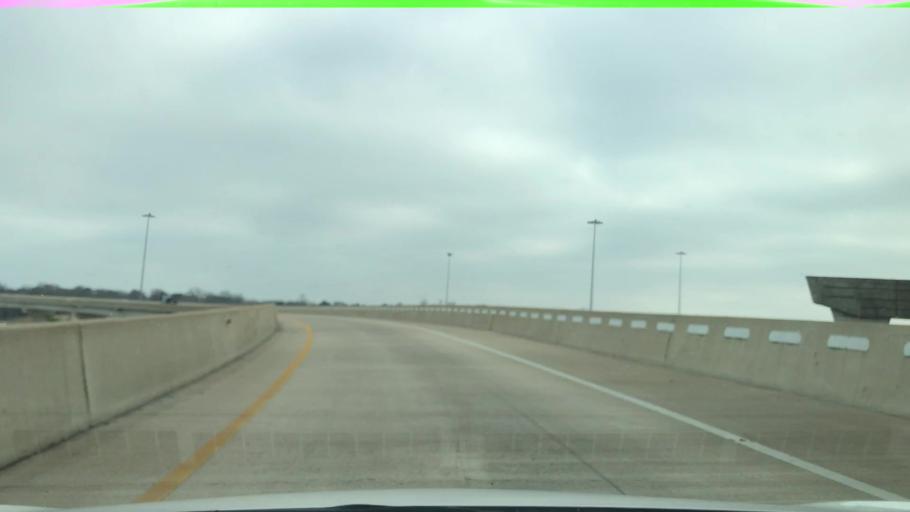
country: US
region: Texas
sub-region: Dallas County
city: Rowlett
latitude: 32.8603
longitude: -96.5553
